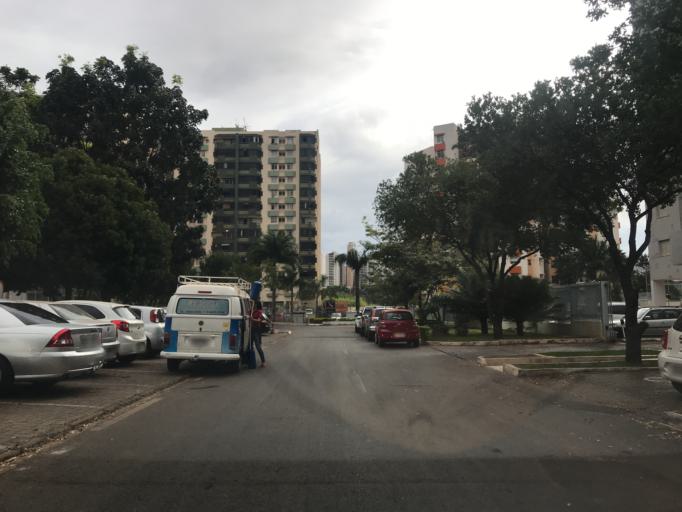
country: BR
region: Federal District
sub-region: Brasilia
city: Brasilia
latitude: -15.8344
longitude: -48.0195
